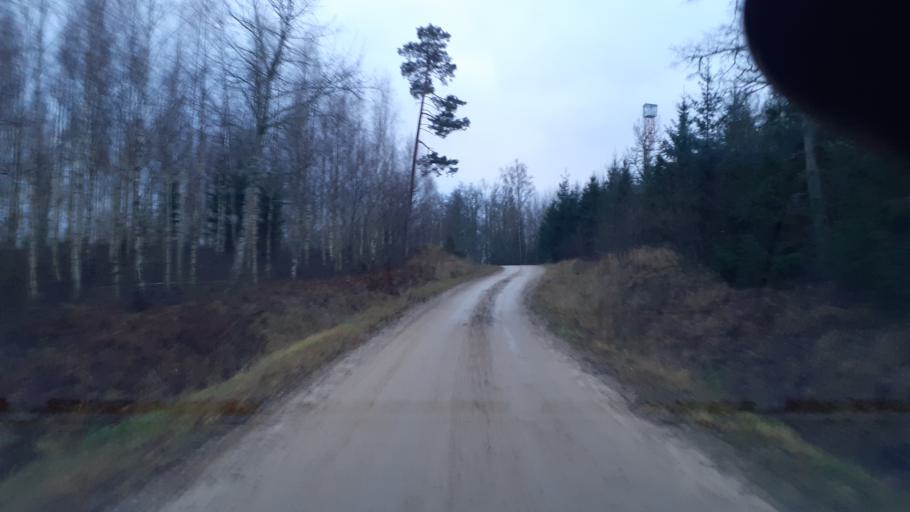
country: LV
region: Alsunga
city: Alsunga
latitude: 56.9091
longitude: 21.7127
